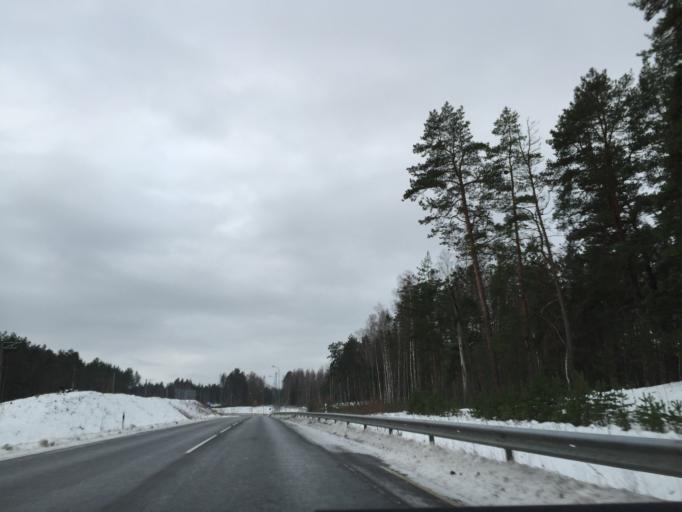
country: LV
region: Saulkrastu
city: Saulkrasti
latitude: 57.1995
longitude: 24.3675
